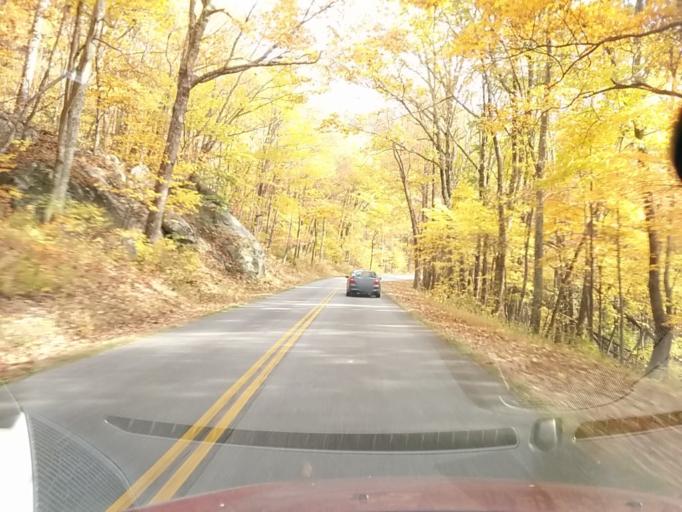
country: US
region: Virginia
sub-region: City of Buena Vista
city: Buena Vista
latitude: 37.8190
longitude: -79.1762
